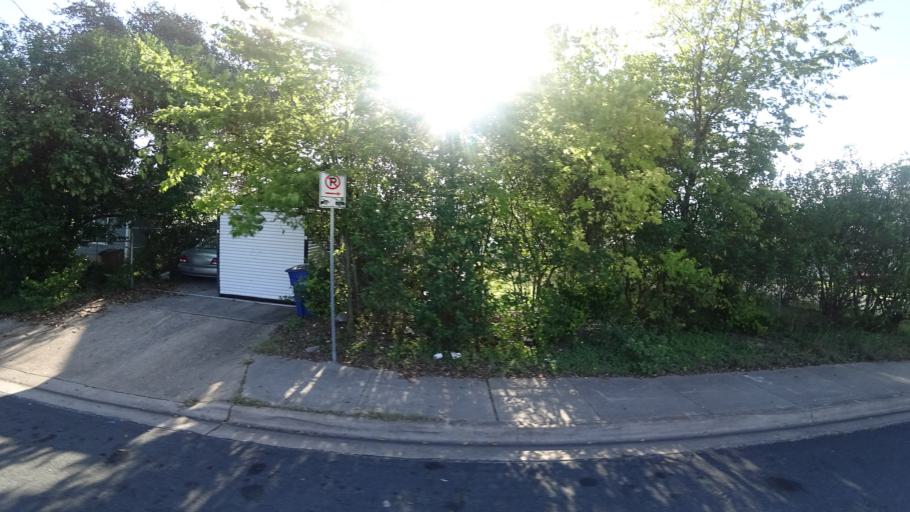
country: US
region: Texas
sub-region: Travis County
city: Austin
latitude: 30.3302
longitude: -97.6982
